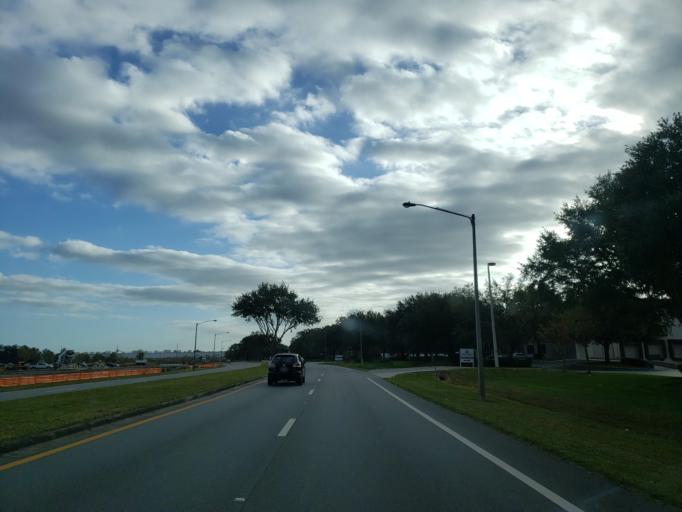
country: US
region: Florida
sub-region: Hillsborough County
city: Plant City
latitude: 27.9895
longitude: -82.1104
